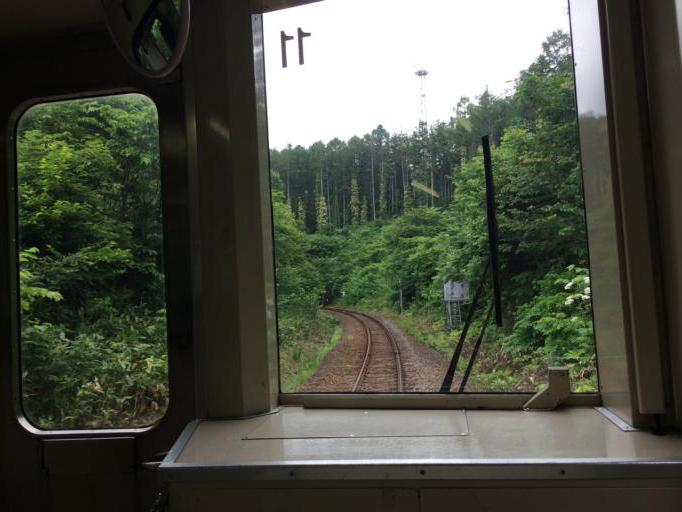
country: JP
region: Hokkaido
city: Otaru
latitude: 43.1974
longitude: 140.8927
